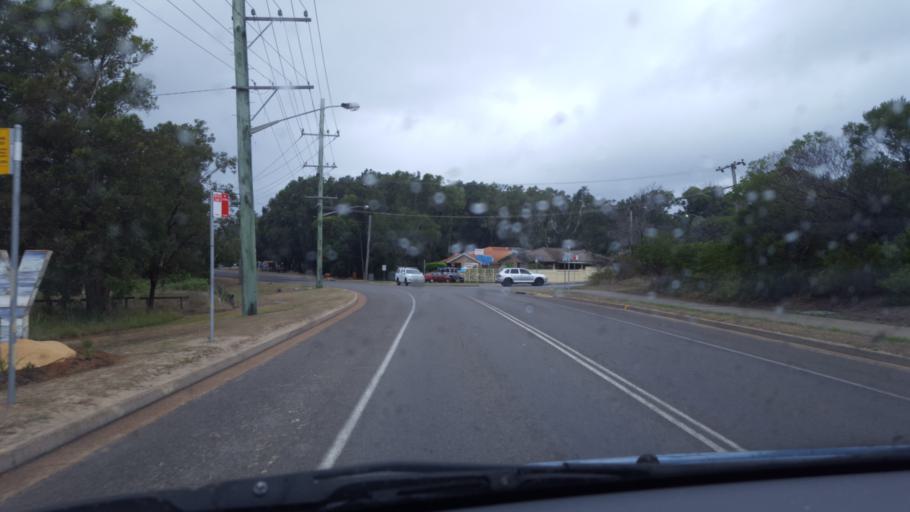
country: AU
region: New South Wales
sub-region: Port Stephens Shire
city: Anna Bay
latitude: -32.7768
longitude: 152.0806
